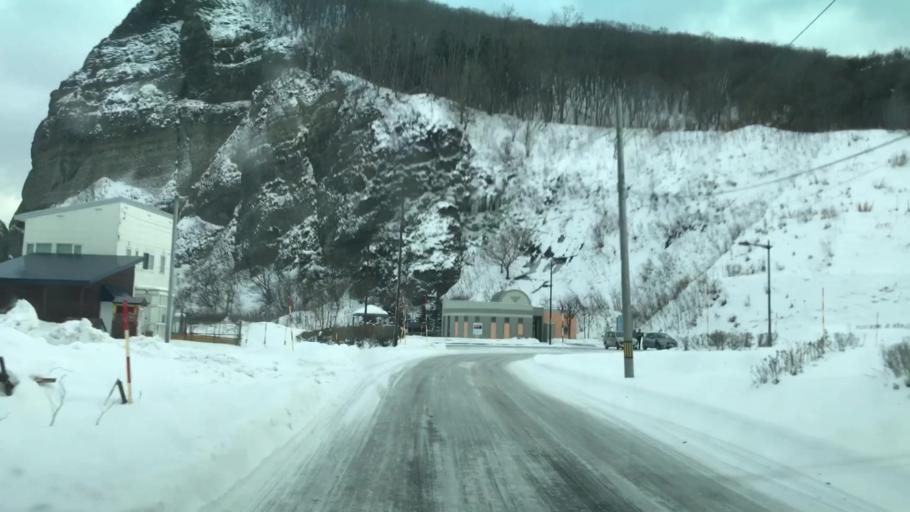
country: JP
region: Hokkaido
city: Yoichi
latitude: 43.2541
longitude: 140.6836
